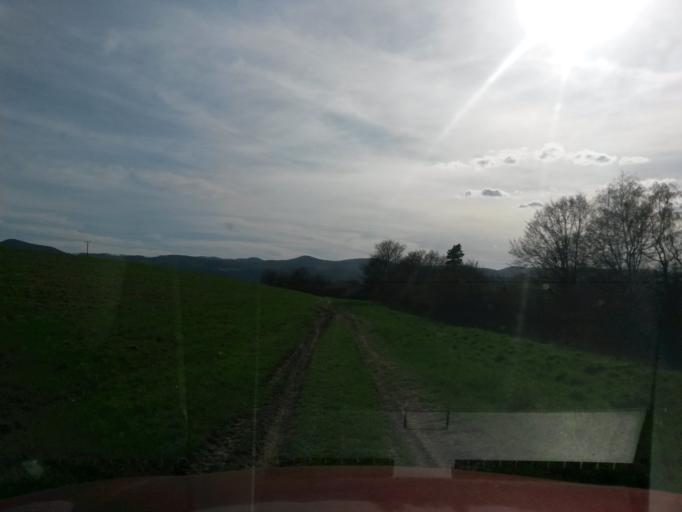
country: SK
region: Presovsky
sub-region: Okres Presov
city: Presov
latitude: 48.9246
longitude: 21.2105
